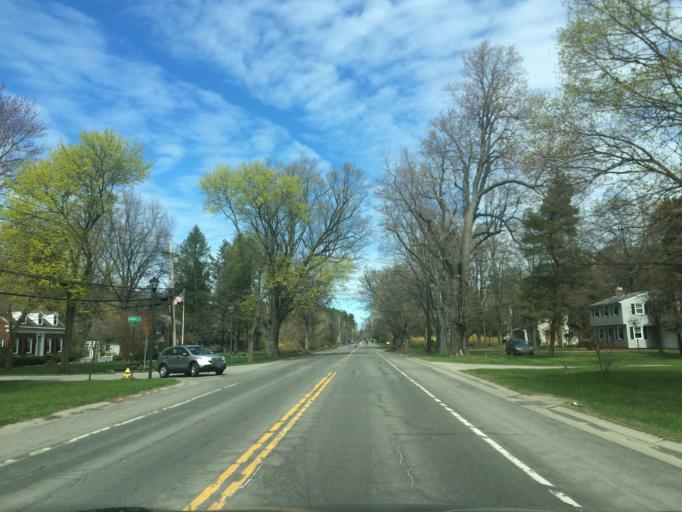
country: US
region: New York
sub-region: Monroe County
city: East Rochester
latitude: 43.0881
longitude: -77.4895
